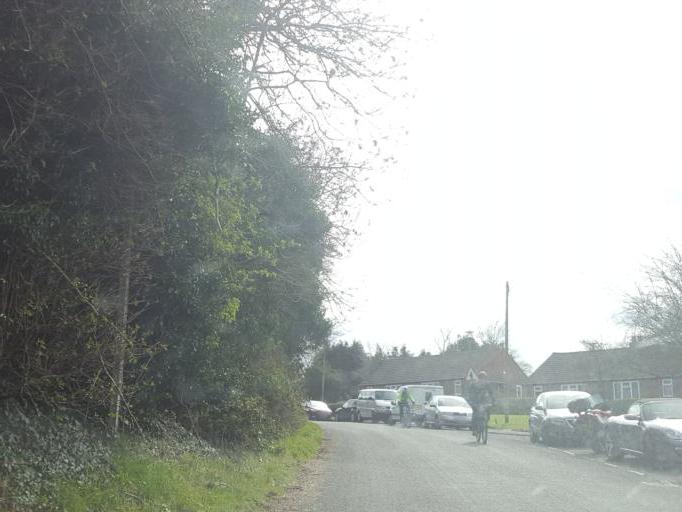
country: GB
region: England
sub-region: Worcestershire
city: Great Malvern
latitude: 52.1201
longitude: -2.3469
